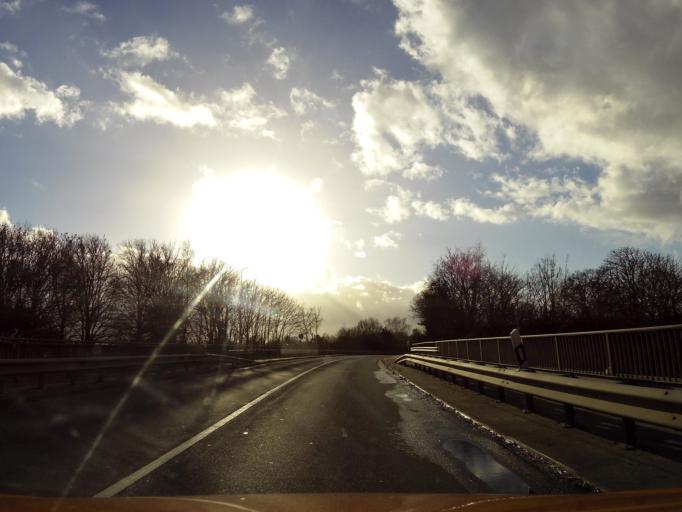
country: DE
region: Lower Saxony
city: Langwedel
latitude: 52.9829
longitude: 9.1787
